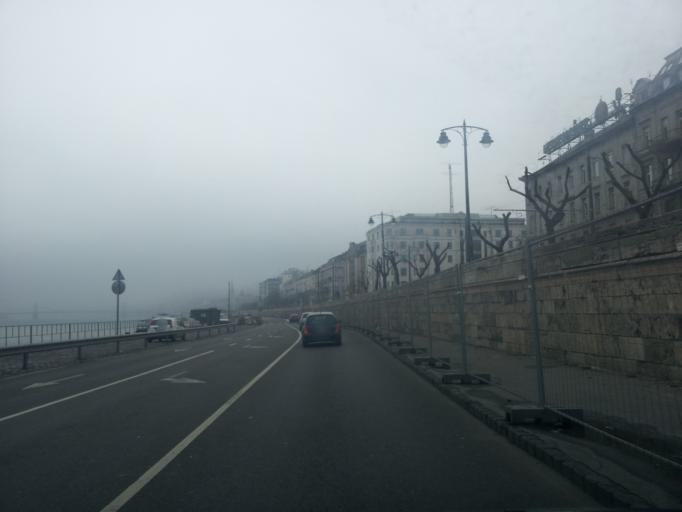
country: HU
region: Budapest
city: Budapest II. keruelet
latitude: 47.5132
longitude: 19.0398
